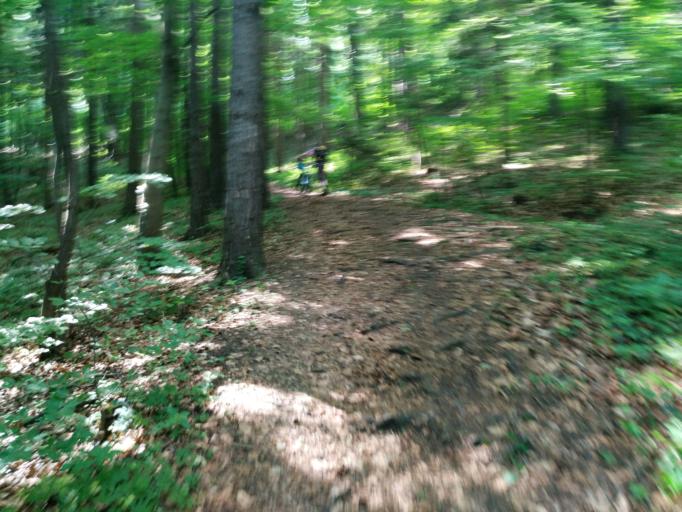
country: AT
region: Styria
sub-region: Graz Stadt
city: Wetzelsdorf
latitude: 47.0372
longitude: 15.3841
